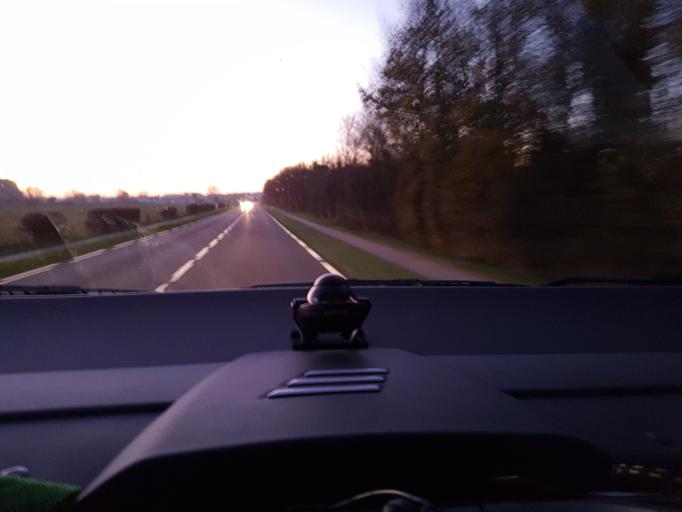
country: FR
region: Picardie
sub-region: Departement de la Somme
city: Saint-Valery-sur-Somme
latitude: 50.1735
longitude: 1.6689
